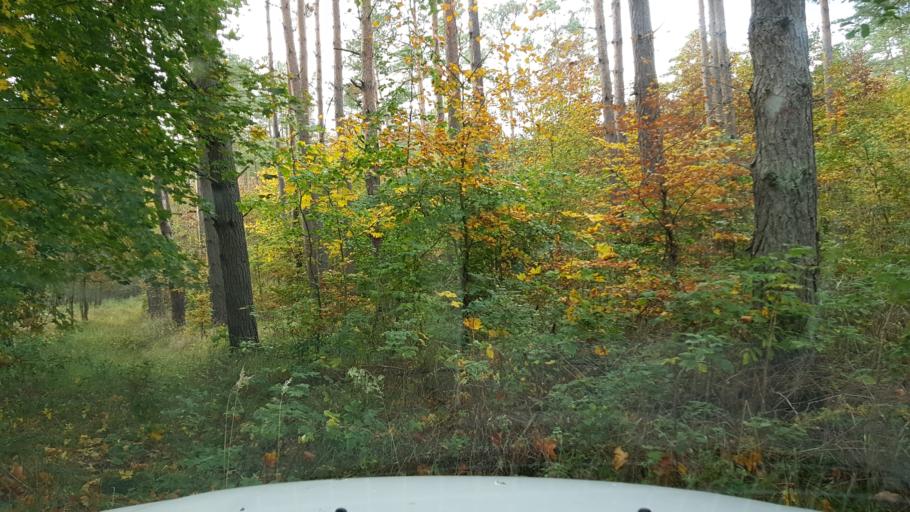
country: PL
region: West Pomeranian Voivodeship
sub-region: Powiat lobeski
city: Wegorzyno
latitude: 53.5287
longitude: 15.5326
